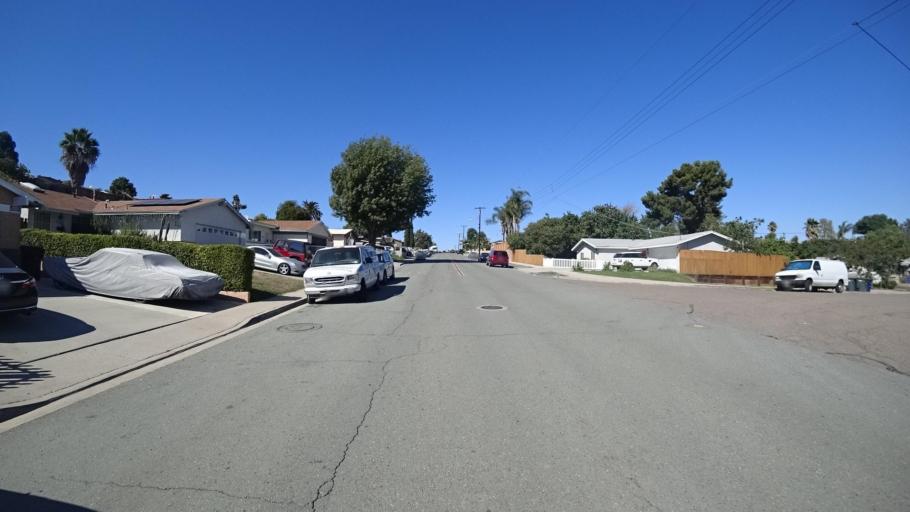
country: US
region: California
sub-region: San Diego County
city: La Presa
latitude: 32.7096
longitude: -117.0187
